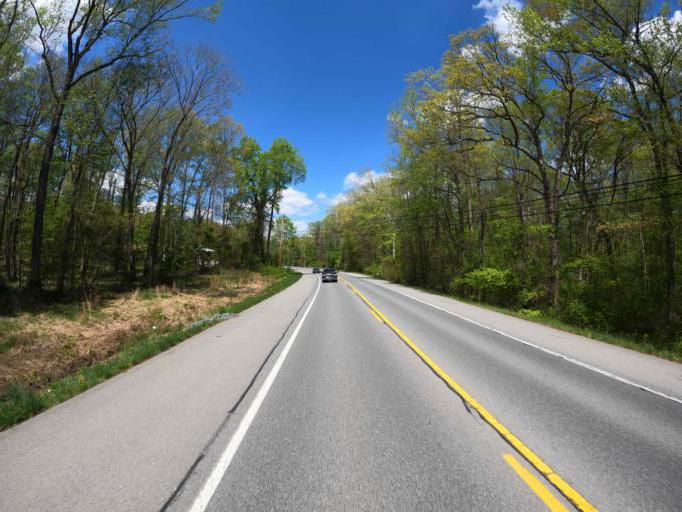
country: US
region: Maryland
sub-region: Charles County
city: Potomac Heights
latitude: 38.5703
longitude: -77.0999
